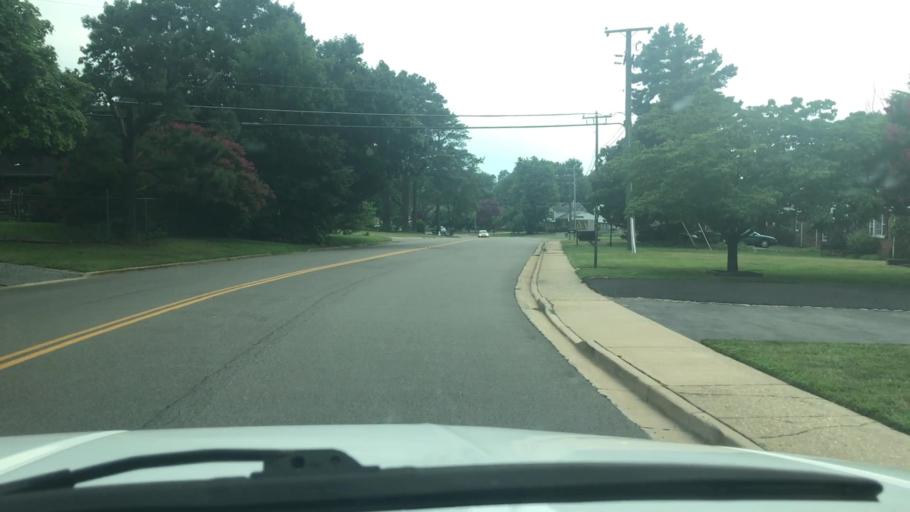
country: US
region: Virginia
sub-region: Henrico County
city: Laurel
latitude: 37.6426
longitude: -77.5429
